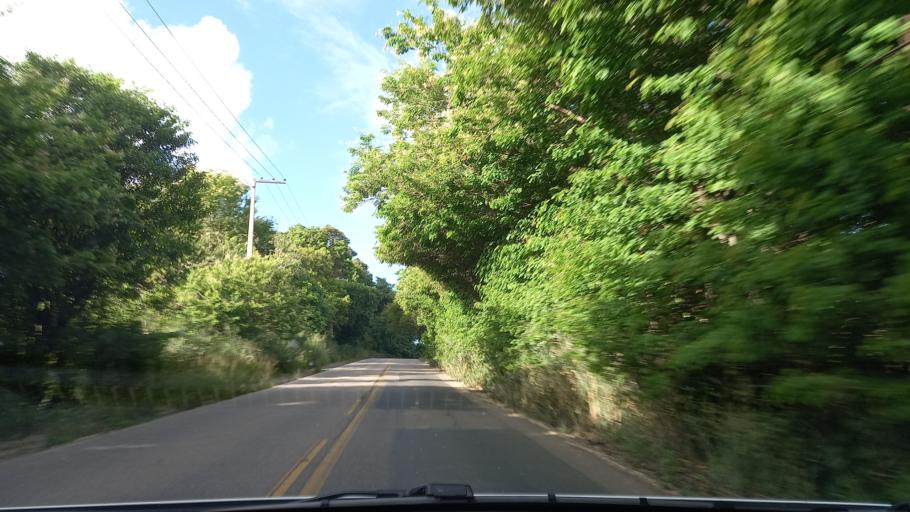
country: BR
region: Pernambuco
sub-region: Rio Formoso
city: Rio Formoso
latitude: -8.6535
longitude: -35.1349
